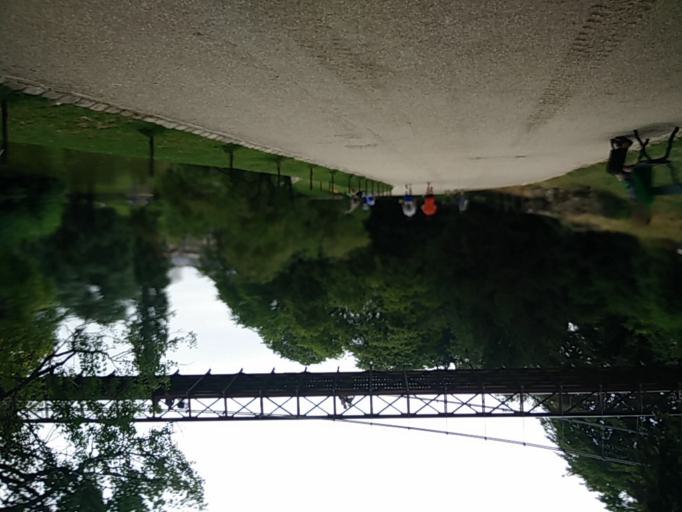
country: FR
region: Ile-de-France
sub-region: Departement de Seine-Saint-Denis
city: Le Pre-Saint-Gervais
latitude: 48.8808
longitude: 2.3816
